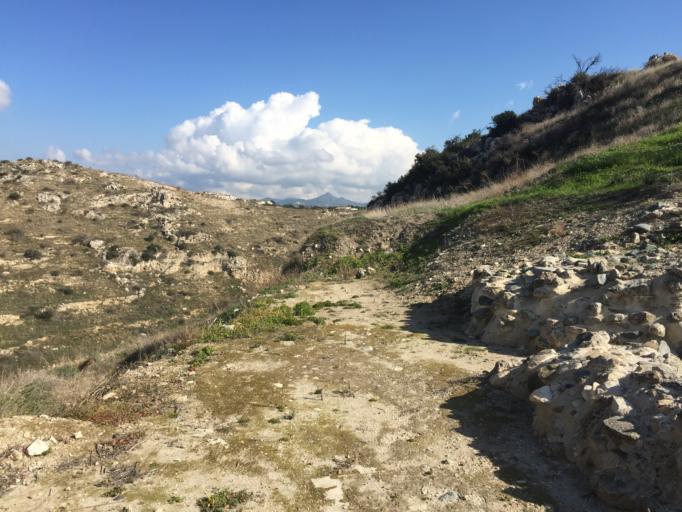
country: CY
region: Larnaka
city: Kofinou
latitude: 34.7973
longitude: 33.3429
